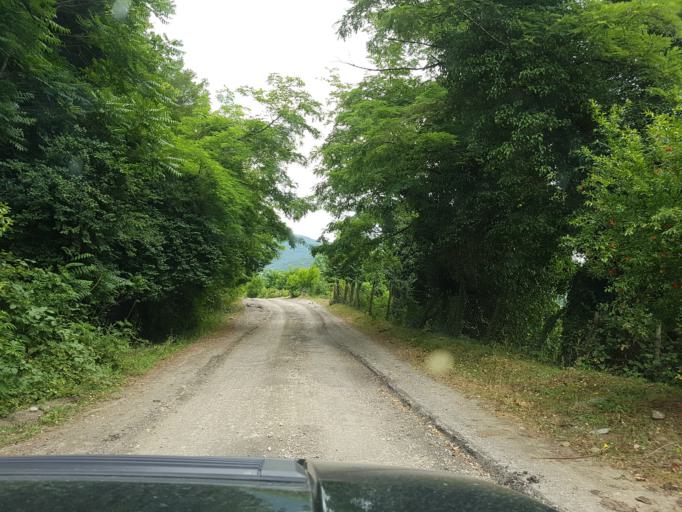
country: GE
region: Imereti
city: Tsqaltubo
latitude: 42.4747
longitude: 42.7484
